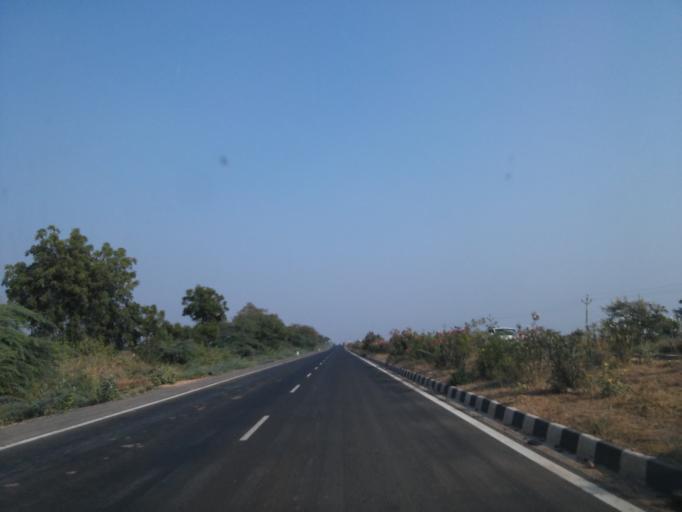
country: IN
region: Gujarat
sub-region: Surendranagar
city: Halvad
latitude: 23.0052
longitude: 71.1118
